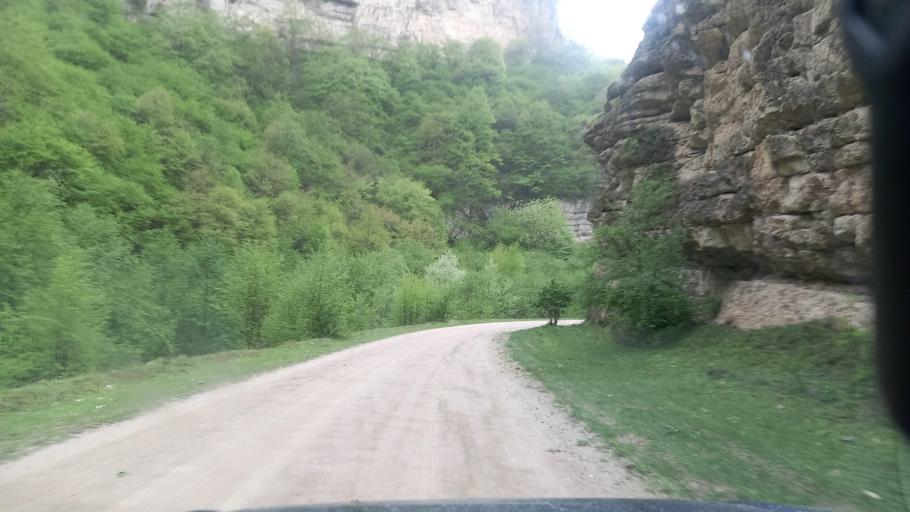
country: RU
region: Kabardino-Balkariya
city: Gundelen
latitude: 43.5936
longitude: 43.1369
